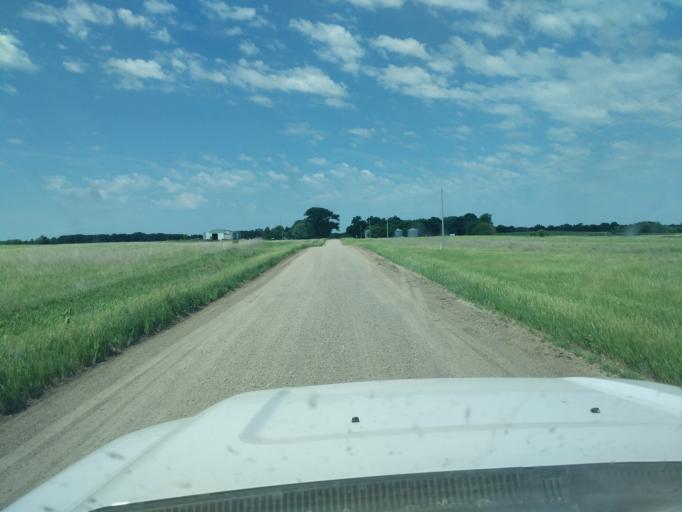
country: US
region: Minnesota
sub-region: Yellow Medicine County
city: Granite Falls
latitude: 44.7453
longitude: -95.3929
